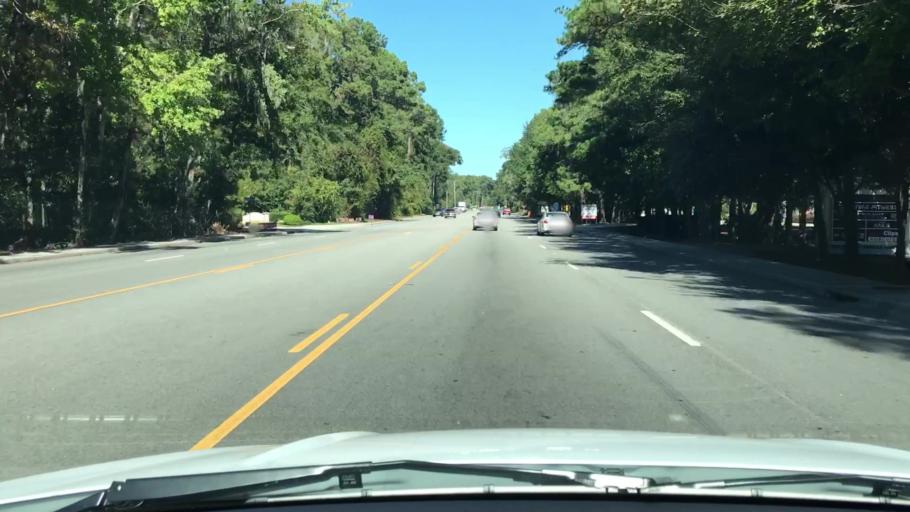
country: US
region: South Carolina
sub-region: Beaufort County
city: Burton
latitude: 32.4279
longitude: -80.7268
